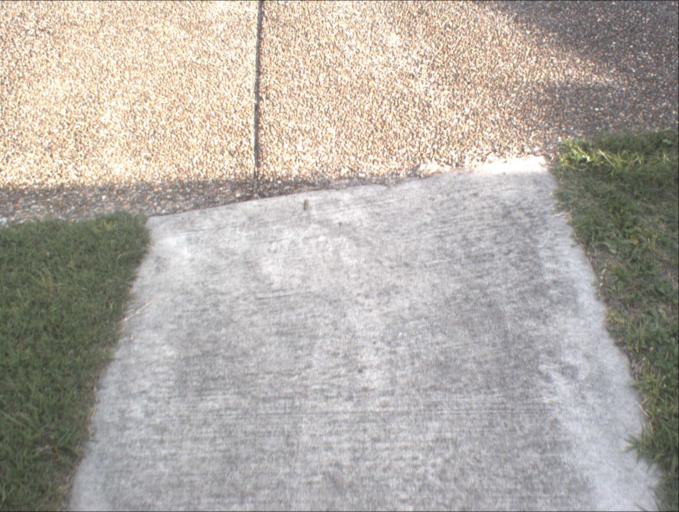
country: AU
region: Queensland
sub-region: Logan
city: Logan Reserve
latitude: -27.6976
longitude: 153.0938
